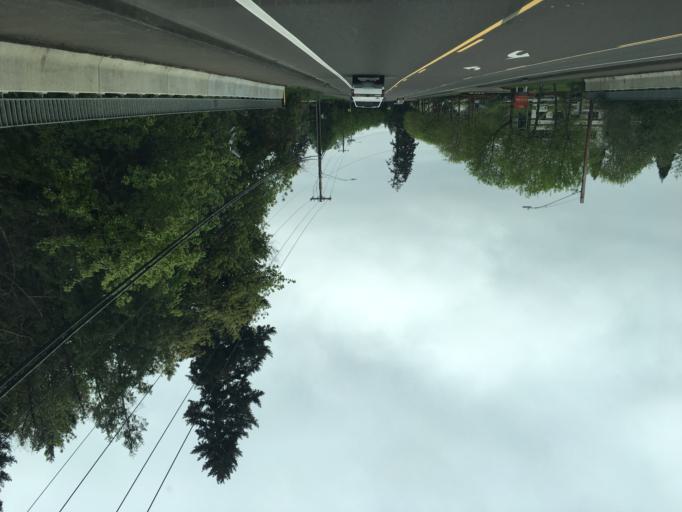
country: US
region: Oregon
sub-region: Washington County
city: Durham
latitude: 45.4032
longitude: -122.7546
